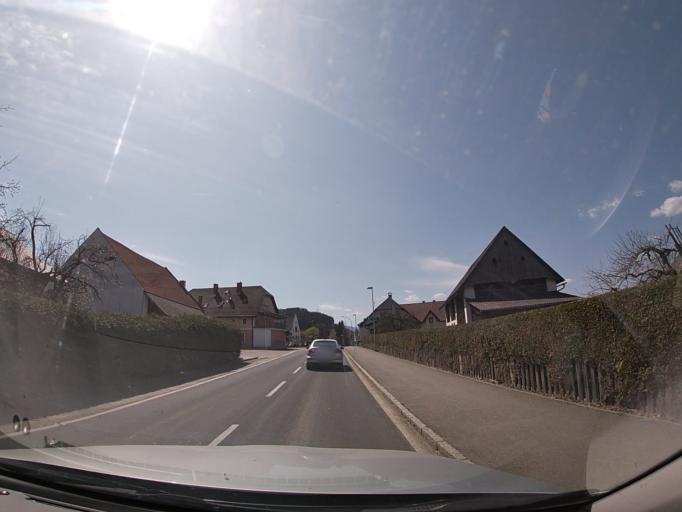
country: AT
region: Styria
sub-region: Politischer Bezirk Murtal
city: Sankt Margarethen bei Knittelfeld
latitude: 47.2278
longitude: 14.8596
